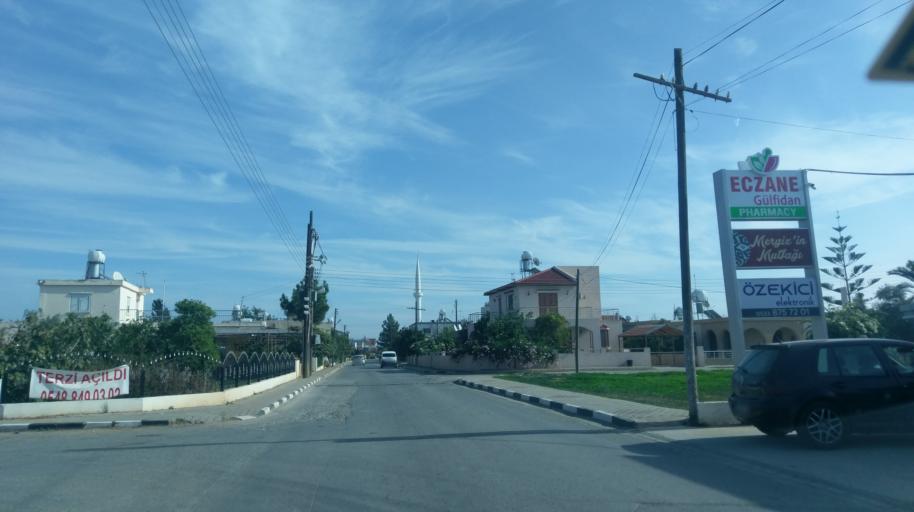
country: CY
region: Ammochostos
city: Trikomo
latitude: 35.1973
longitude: 33.8682
